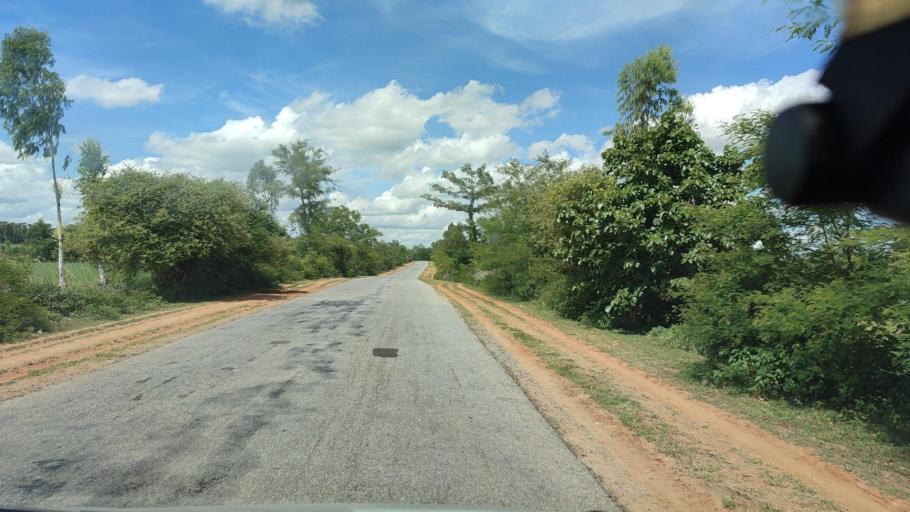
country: MM
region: Magway
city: Magway
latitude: 20.1945
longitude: 95.2136
